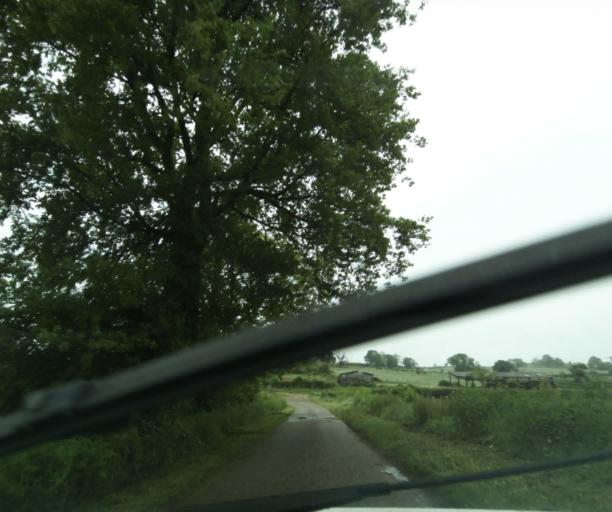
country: FR
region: Bourgogne
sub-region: Departement de Saone-et-Loire
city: Charolles
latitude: 46.4086
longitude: 4.3884
